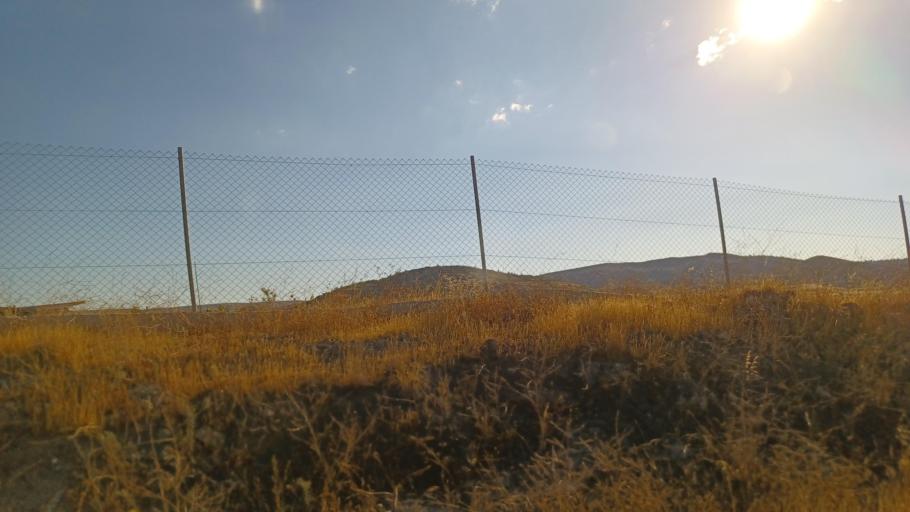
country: CY
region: Larnaka
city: Troulloi
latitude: 35.0117
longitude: 33.6352
